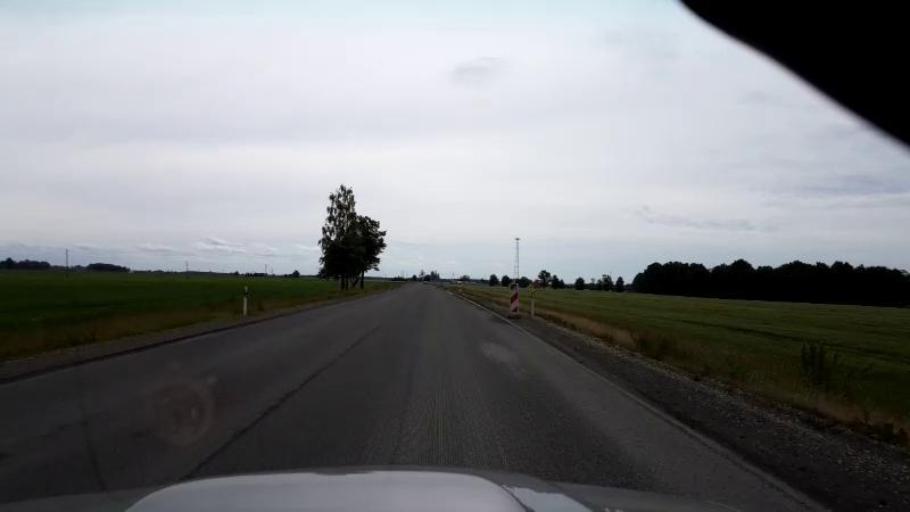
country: LV
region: Bauskas Rajons
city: Bauska
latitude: 56.2928
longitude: 24.3507
